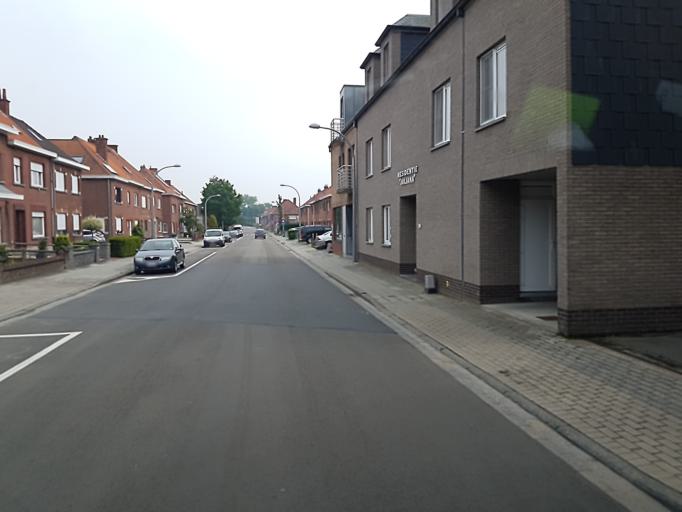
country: BE
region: Flanders
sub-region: Provincie West-Vlaanderen
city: Kortrijk
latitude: 50.8205
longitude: 3.2296
